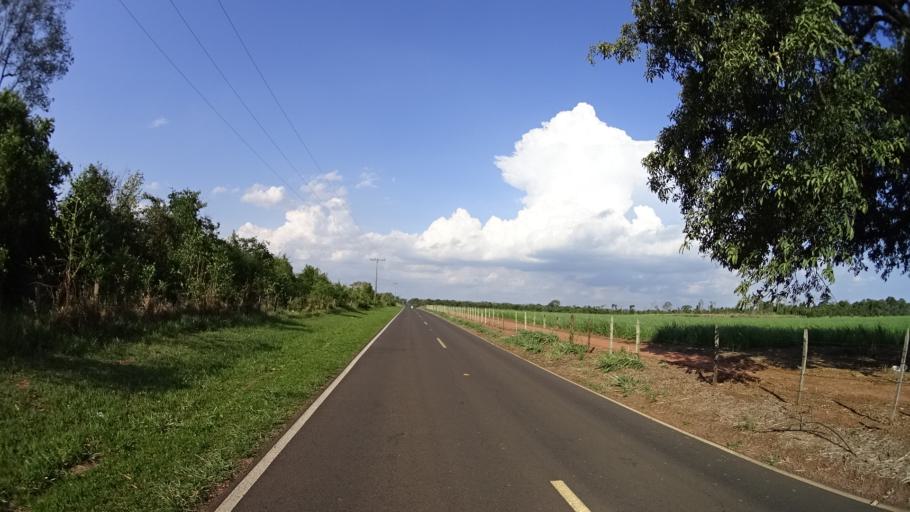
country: BR
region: Sao Paulo
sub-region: Urupes
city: Urupes
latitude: -21.3837
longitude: -49.4924
